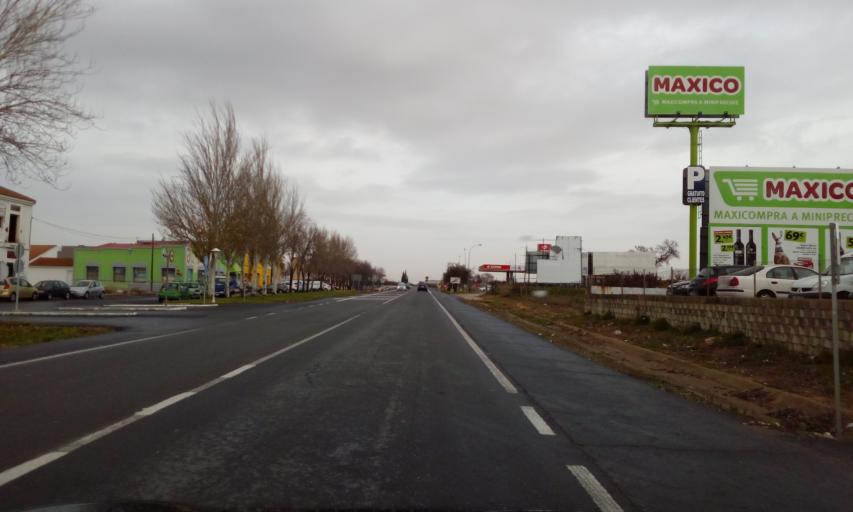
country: ES
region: Andalusia
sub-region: Provincia de Huelva
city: Lepe
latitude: 37.2628
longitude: -7.1963
